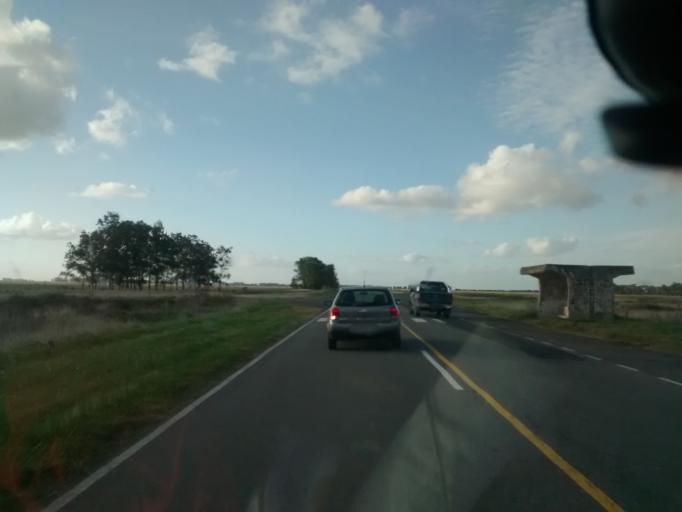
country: AR
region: Buenos Aires
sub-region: Partido de General Belgrano
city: General Belgrano
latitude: -36.1893
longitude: -58.5931
